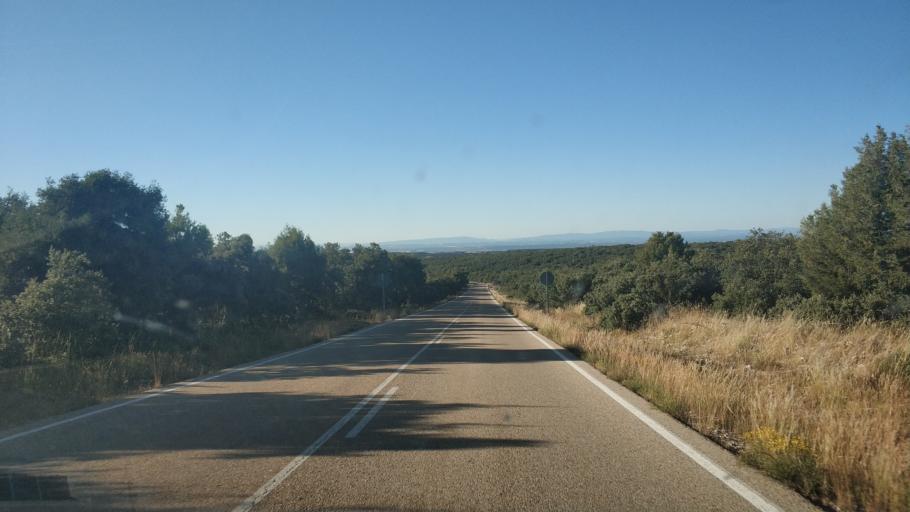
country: ES
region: Castille and Leon
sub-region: Provincia de Soria
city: Montejo de Tiermes
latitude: 41.4074
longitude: -3.2019
